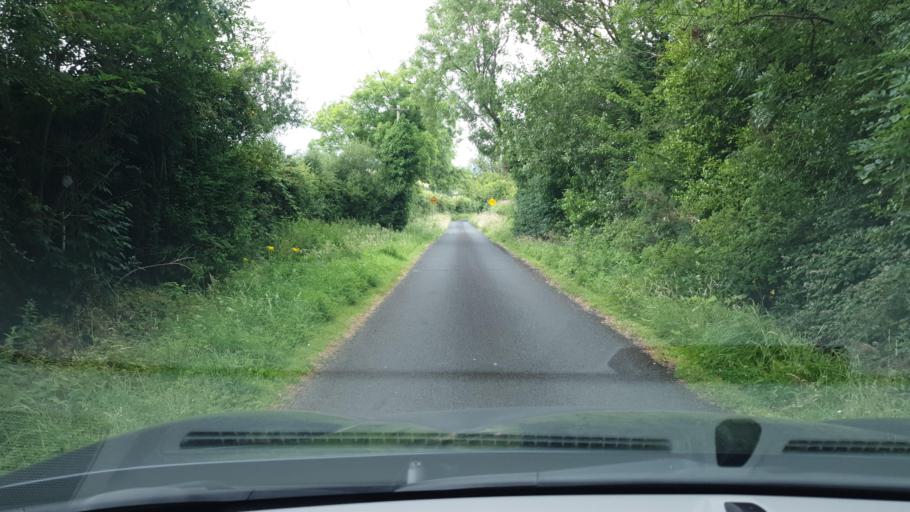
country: IE
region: Leinster
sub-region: An Mhi
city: Ashbourne
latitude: 53.5694
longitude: -6.3958
